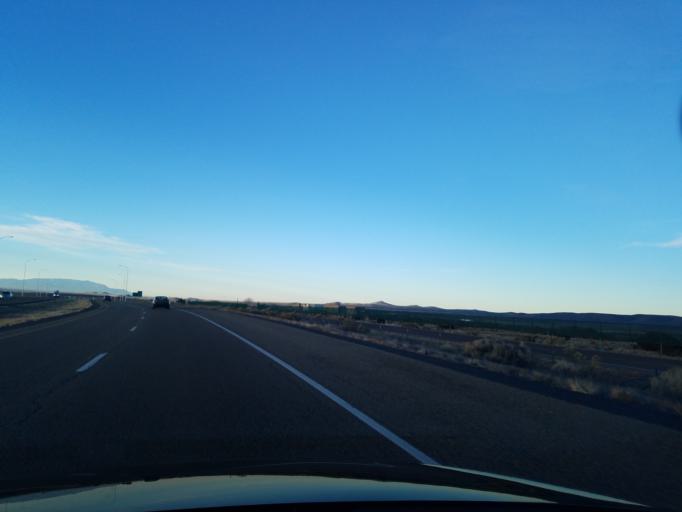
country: US
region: New Mexico
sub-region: Santa Fe County
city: Agua Fria
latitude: 35.6642
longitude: -106.0313
